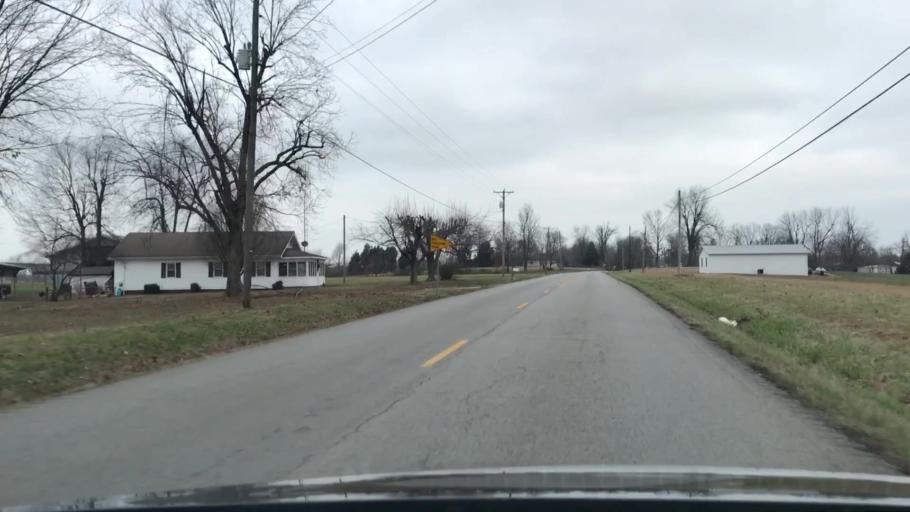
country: US
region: Kentucky
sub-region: McLean County
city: Calhoun
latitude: 37.3972
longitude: -87.2579
